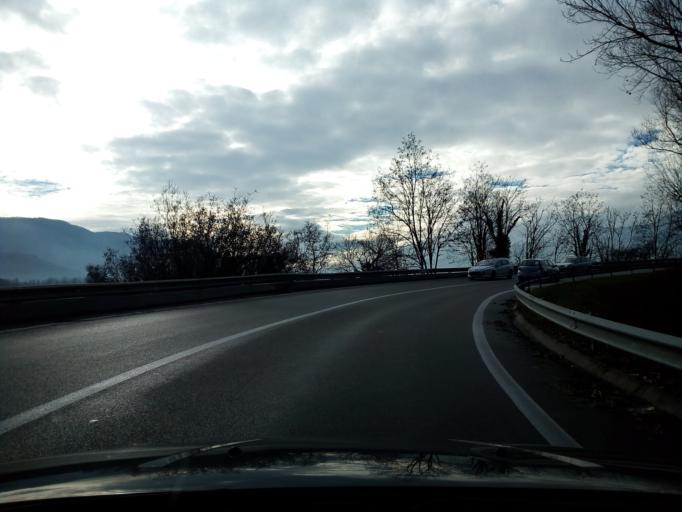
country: FR
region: Rhone-Alpes
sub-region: Departement de l'Isere
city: Meylan
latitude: 45.2053
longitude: 5.7942
